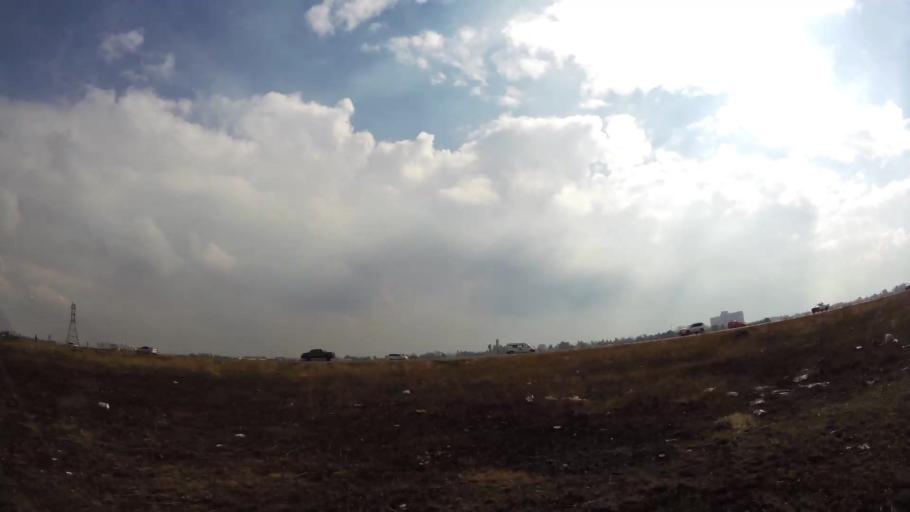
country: ZA
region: Gauteng
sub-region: Sedibeng District Municipality
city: Vereeniging
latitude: -26.6652
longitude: 27.9123
